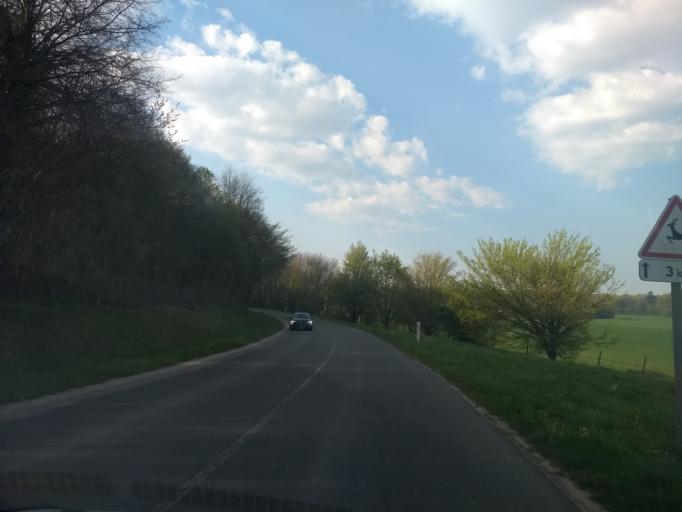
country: FR
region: Picardie
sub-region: Departement de la Somme
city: Albert
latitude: 50.0747
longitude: 2.5949
